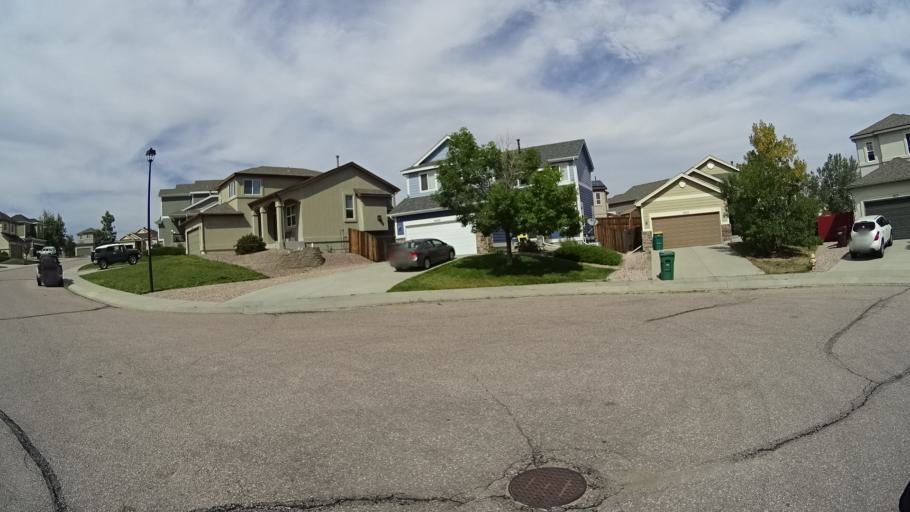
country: US
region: Colorado
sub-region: El Paso County
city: Cimarron Hills
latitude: 38.9083
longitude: -104.7078
